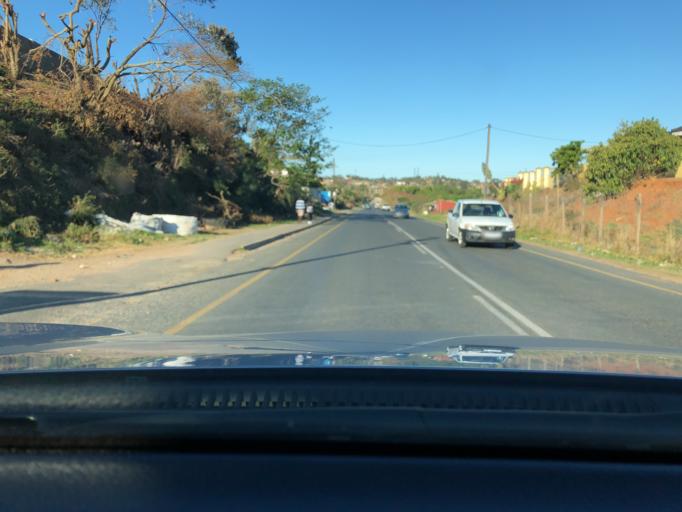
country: ZA
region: KwaZulu-Natal
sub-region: eThekwini Metropolitan Municipality
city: Umkomaas
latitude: -30.0361
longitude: 30.8585
